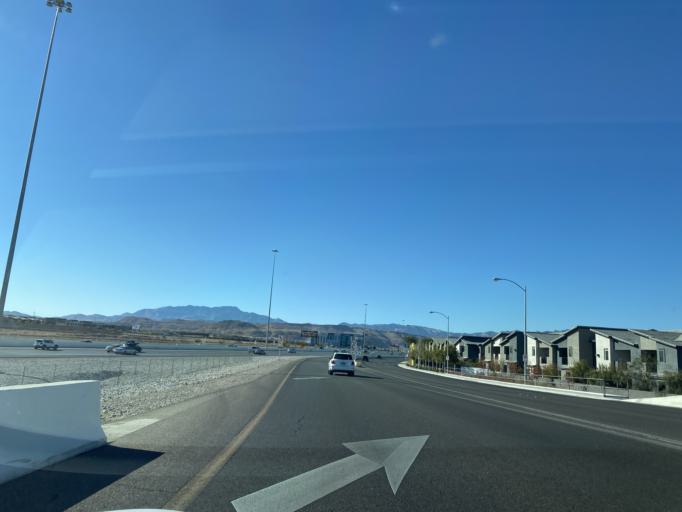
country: US
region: Nevada
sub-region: Clark County
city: Spring Valley
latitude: 36.0669
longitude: -115.2624
